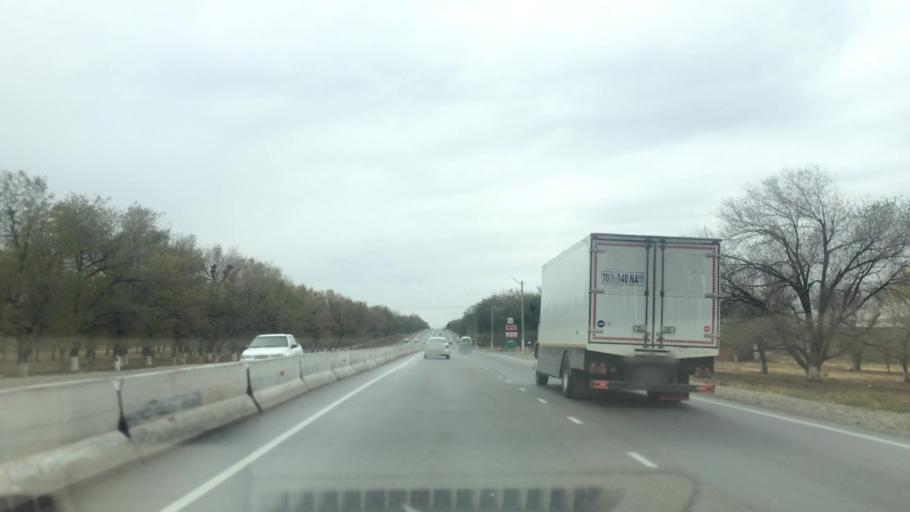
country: UZ
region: Samarqand
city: Bulung'ur
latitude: 39.8963
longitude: 67.4978
